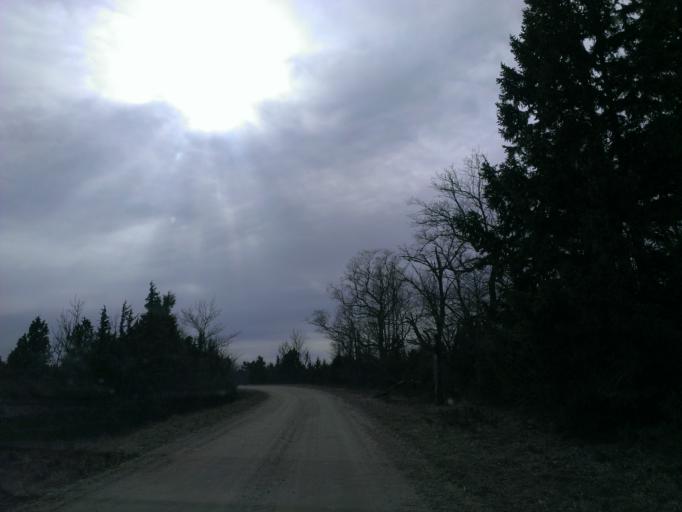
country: EE
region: Laeaene
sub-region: Lihula vald
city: Lihula
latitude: 58.5694
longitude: 23.5473
